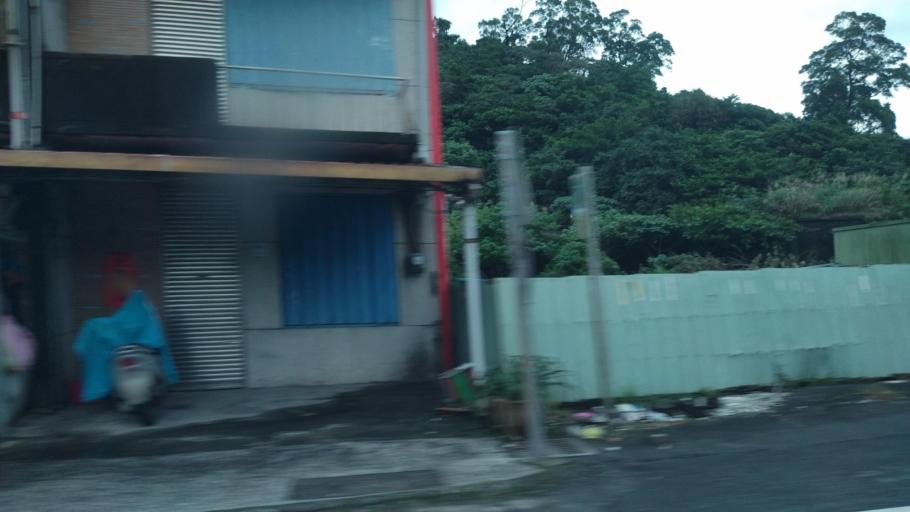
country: TW
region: Taiwan
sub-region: Yilan
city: Yilan
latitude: 24.5971
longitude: 121.8356
